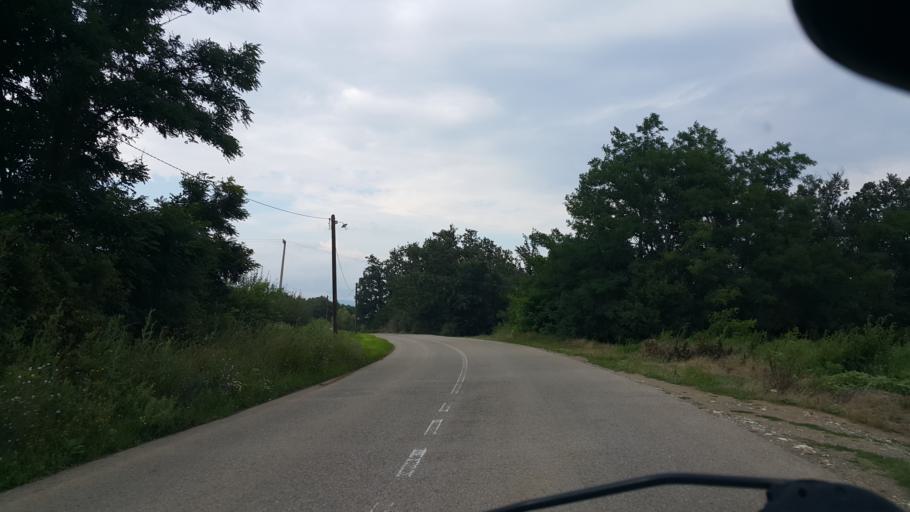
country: RS
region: Central Serbia
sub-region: Toplicki Okrug
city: Blace
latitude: 43.2526
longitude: 21.2643
